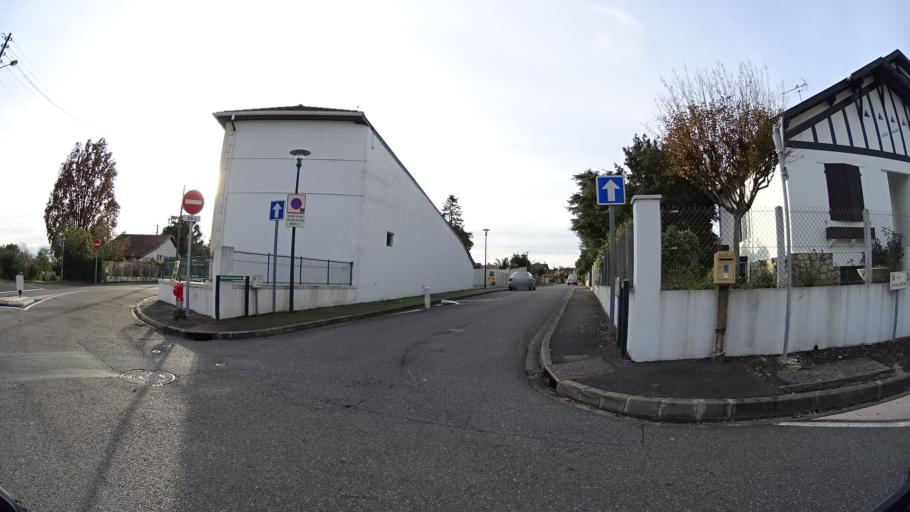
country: FR
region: Aquitaine
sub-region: Departement des Landes
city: Saint-Paul-les-Dax
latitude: 43.7223
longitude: -1.0465
